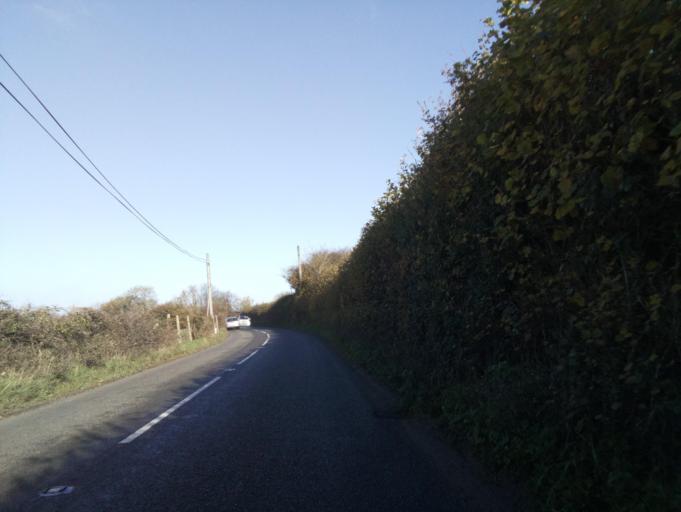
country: GB
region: England
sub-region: Somerset
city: Bruton
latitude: 51.1561
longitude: -2.4171
